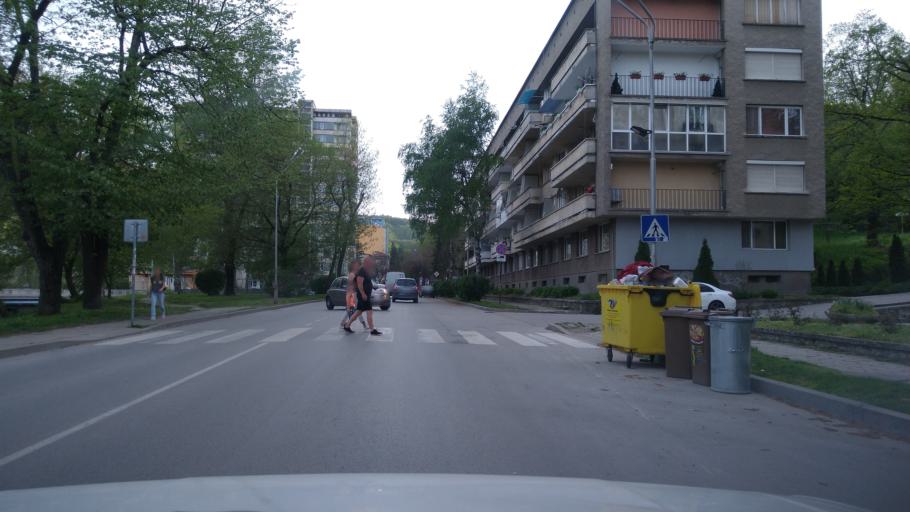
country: BG
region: Gabrovo
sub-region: Obshtina Gabrovo
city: Gabrovo
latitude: 42.8722
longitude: 25.3143
